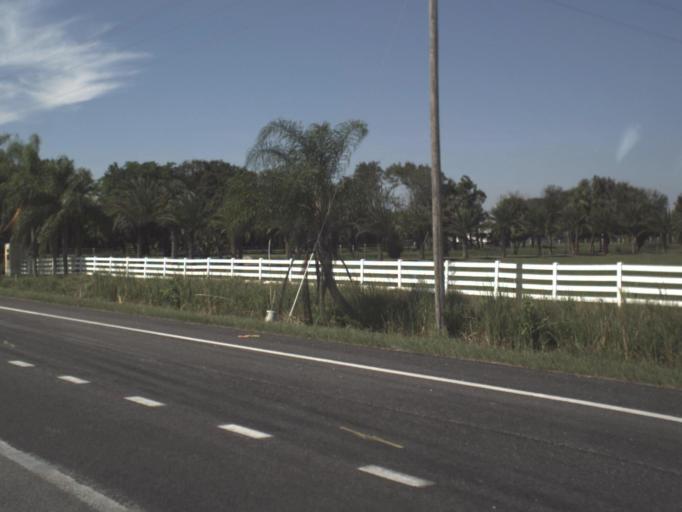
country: US
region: Florida
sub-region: Hendry County
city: Harlem
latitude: 26.7544
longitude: -80.9900
